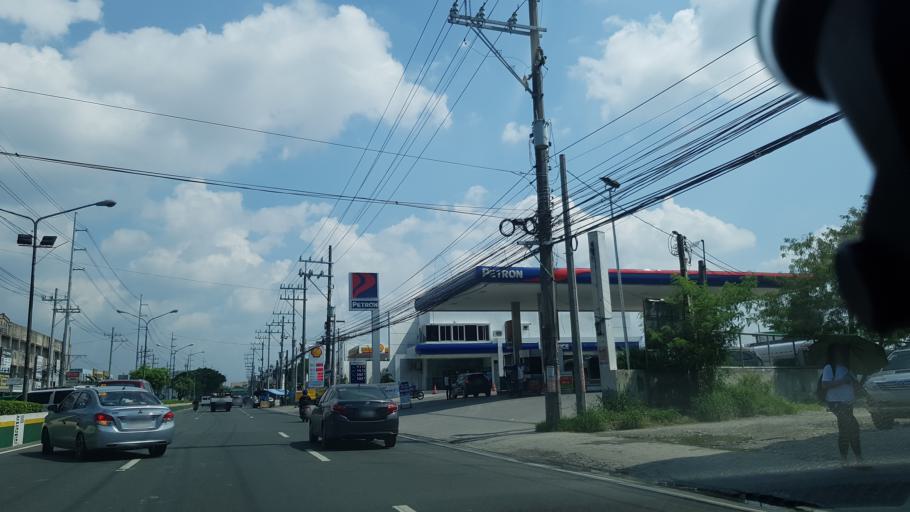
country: PH
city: Sambayanihan People's Village
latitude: 14.4830
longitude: 120.9952
